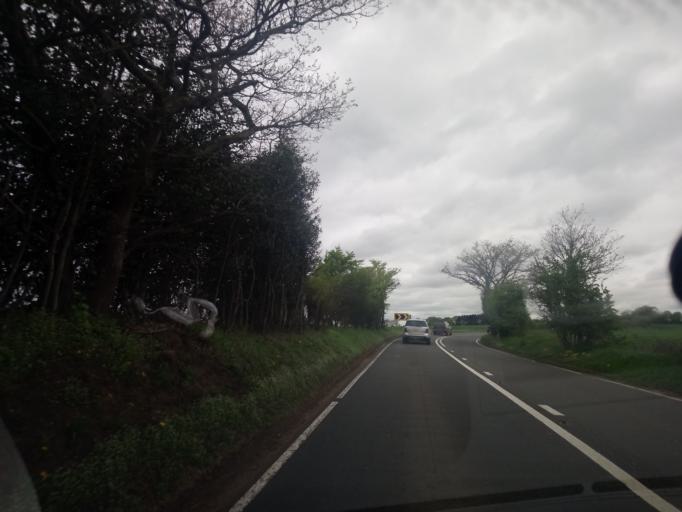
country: GB
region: England
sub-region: Telford and Wrekin
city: Chetwynd
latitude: 52.8180
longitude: -2.4490
